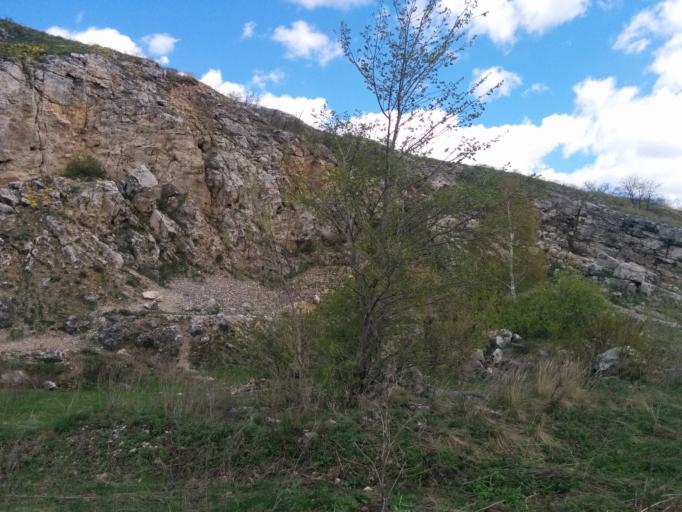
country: RU
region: Bashkortostan
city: Sterlitamak
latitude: 53.7379
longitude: 56.0928
